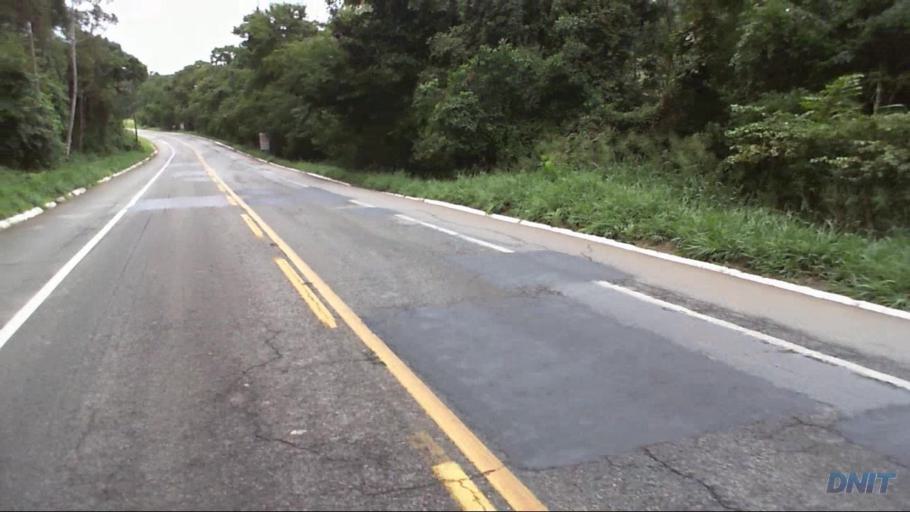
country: BR
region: Minas Gerais
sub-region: Barao De Cocais
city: Barao de Cocais
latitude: -19.8034
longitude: -43.4086
